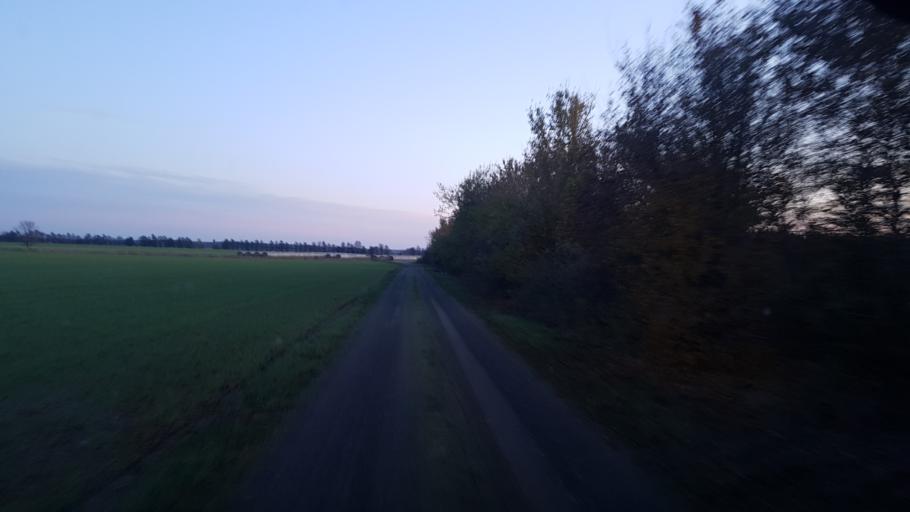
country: DE
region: Brandenburg
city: Schilda
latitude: 51.6293
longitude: 13.3289
